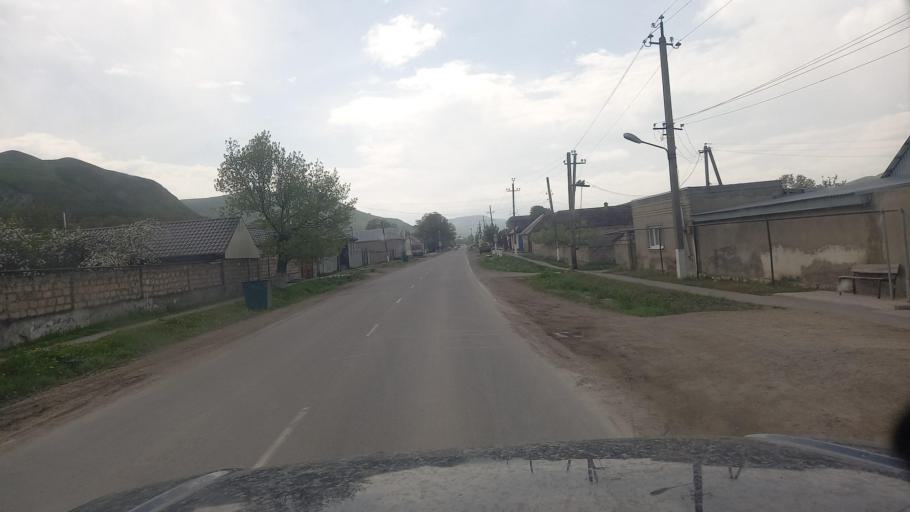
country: RU
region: Kabardino-Balkariya
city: Sarmakovo
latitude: 43.7306
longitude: 43.1654
